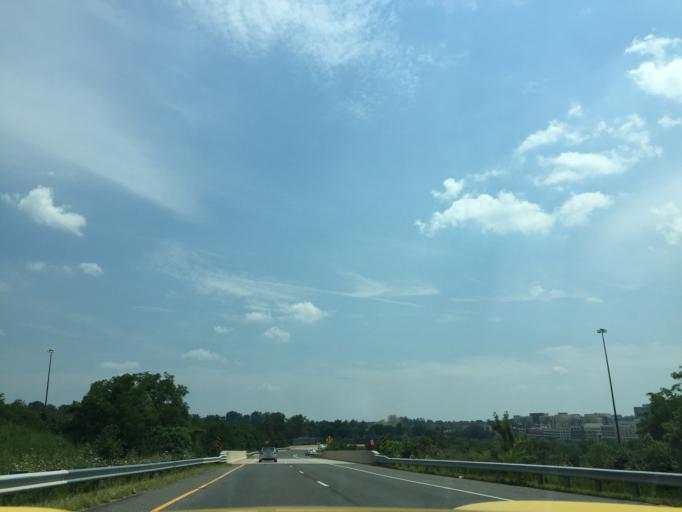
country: US
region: Maryland
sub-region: Prince George's County
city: Forest Heights
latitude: 38.7936
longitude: -77.0157
